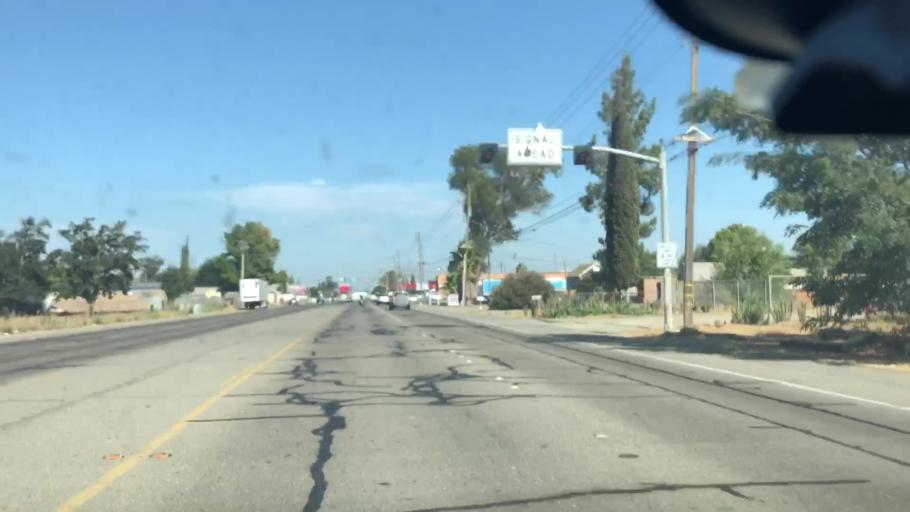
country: US
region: California
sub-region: San Joaquin County
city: Lathrop
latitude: 37.7973
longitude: -121.2556
